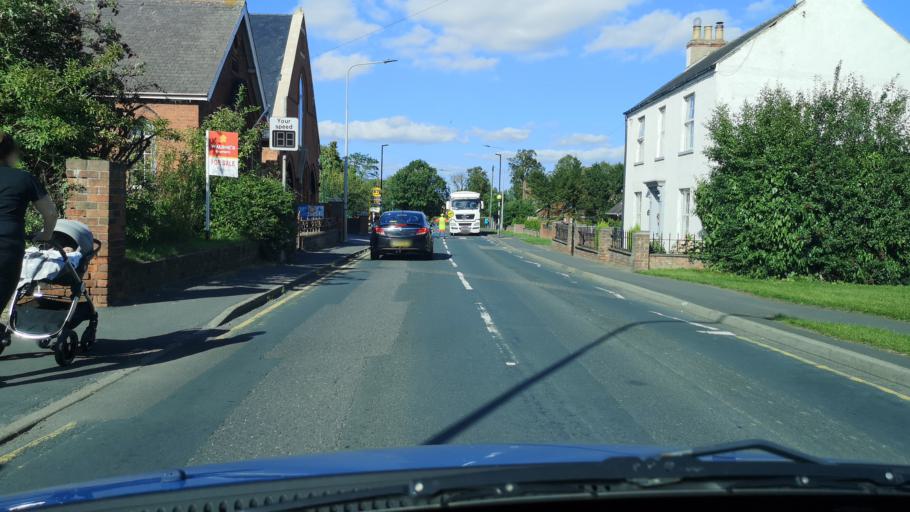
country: GB
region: England
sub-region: North Lincolnshire
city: Belton
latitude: 53.5546
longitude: -0.8159
